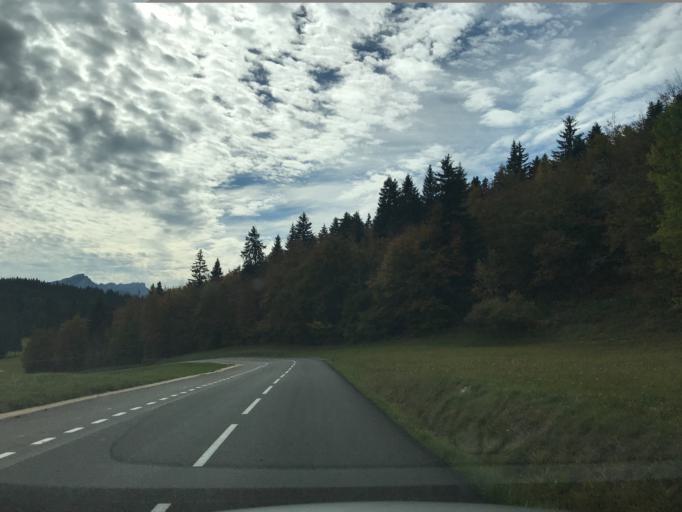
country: FR
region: Rhone-Alpes
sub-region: Departement de la Savoie
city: Vimines
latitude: 45.4581
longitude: 5.8578
